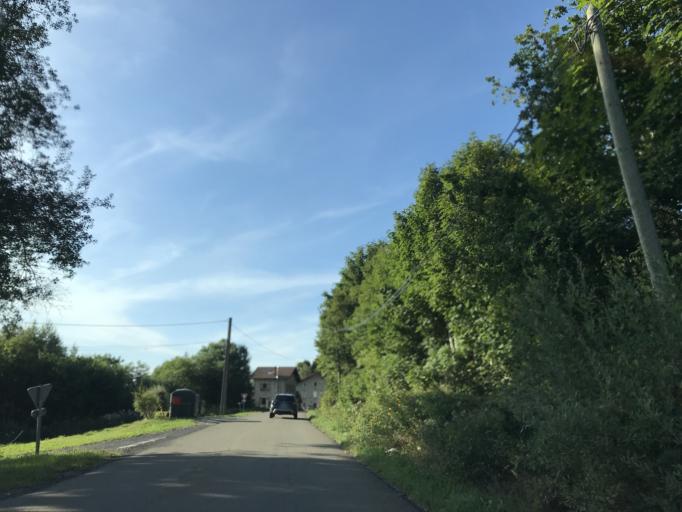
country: FR
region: Auvergne
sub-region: Departement du Puy-de-Dome
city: Job
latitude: 45.7049
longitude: 3.7212
